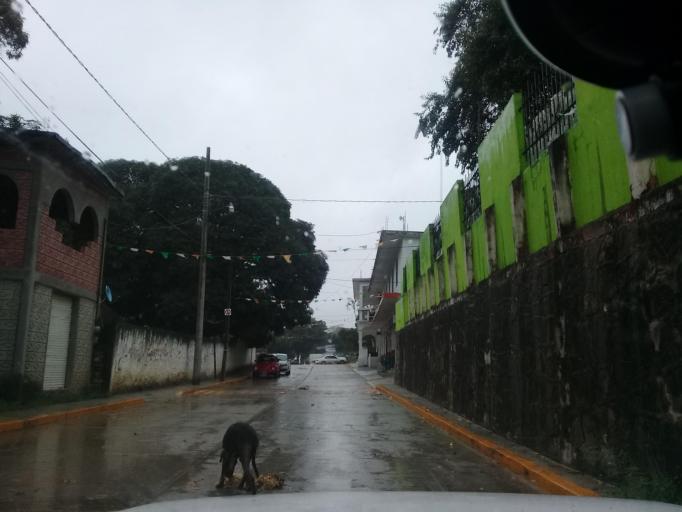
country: MX
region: Veracruz
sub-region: Chalma
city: San Pedro Coyutla
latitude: 21.2298
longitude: -98.4600
